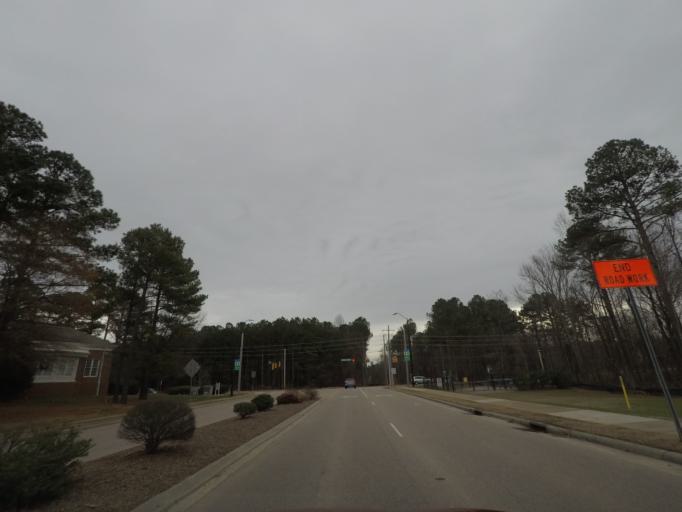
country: US
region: North Carolina
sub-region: Wake County
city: Morrisville
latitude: 35.8221
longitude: -78.8289
